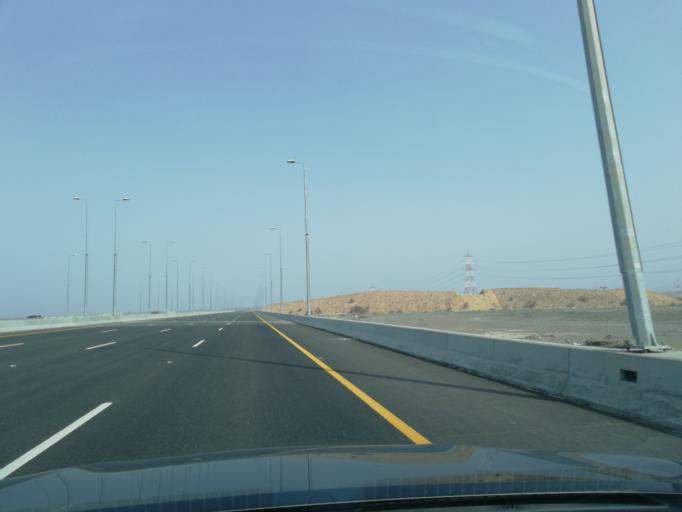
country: OM
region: Al Batinah
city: Al Sohar
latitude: 24.3244
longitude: 56.5678
